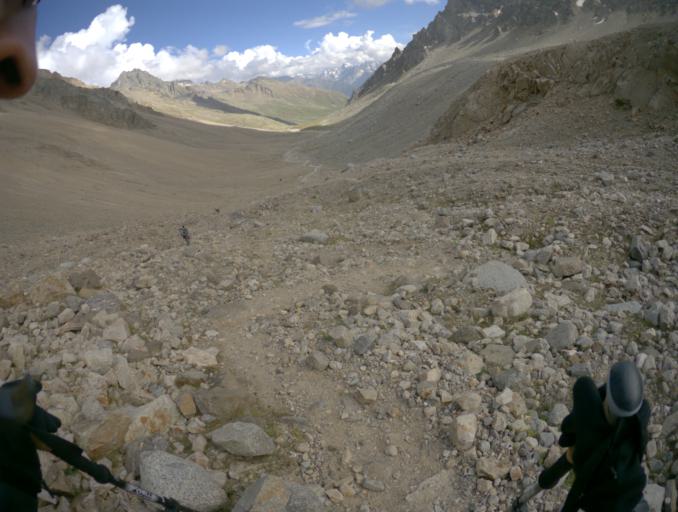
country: RU
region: Kabardino-Balkariya
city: Terskol
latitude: 43.3354
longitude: 42.5530
